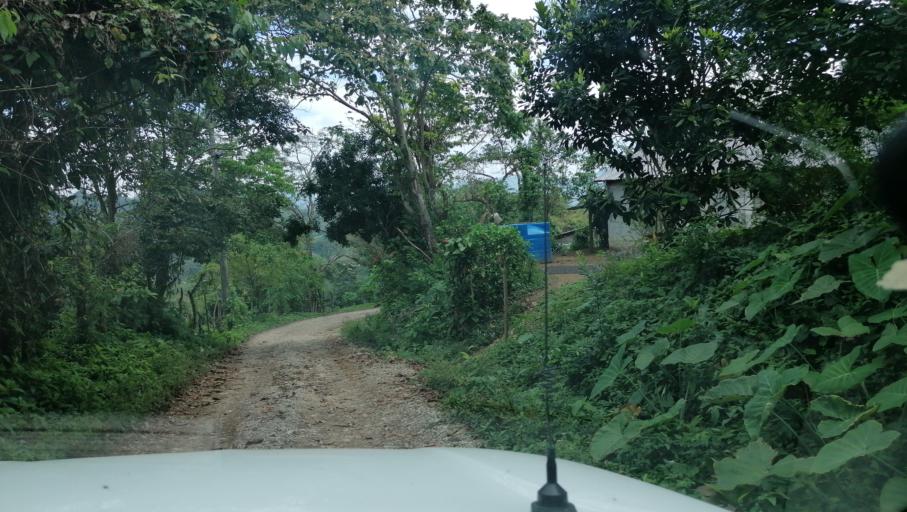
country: MX
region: Chiapas
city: Ixtacomitan
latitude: 17.3582
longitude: -93.1177
